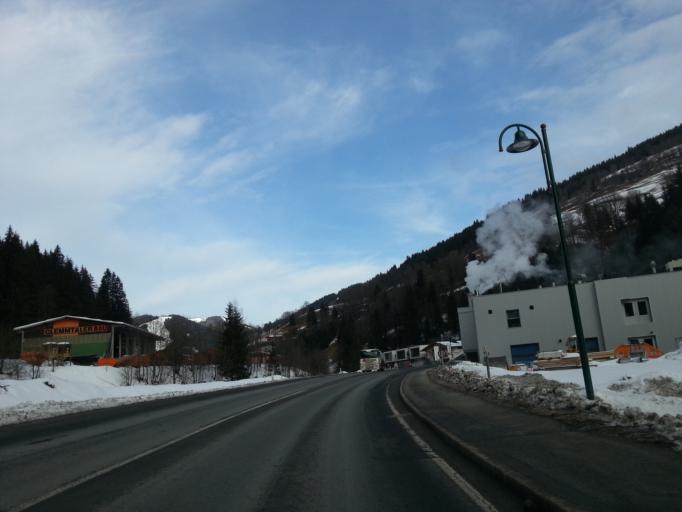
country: AT
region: Salzburg
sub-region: Politischer Bezirk Zell am See
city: Saalbach
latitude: 47.3813
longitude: 12.6682
